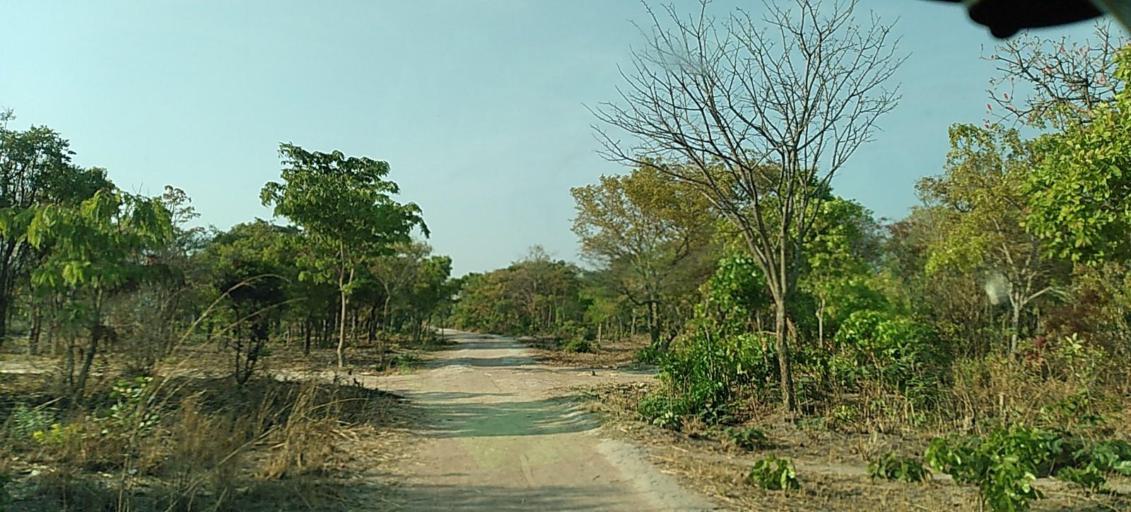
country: ZM
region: North-Western
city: Kalengwa
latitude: -13.1586
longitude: 25.0341
